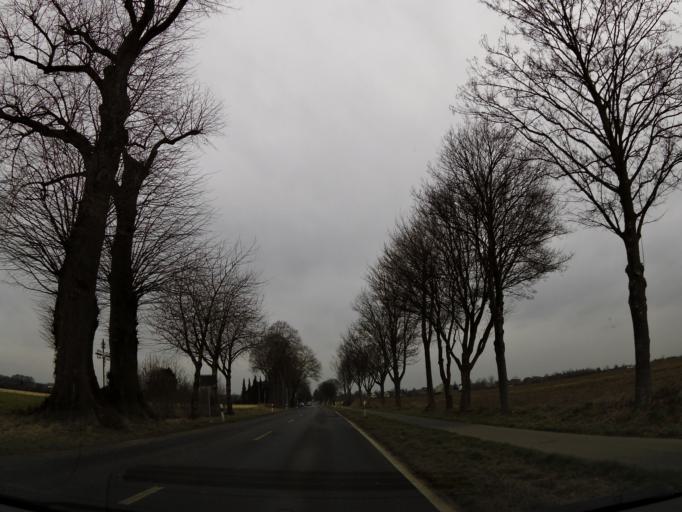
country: NL
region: Limburg
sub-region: Gemeente Schinnen
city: Doenrade
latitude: 50.9958
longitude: 5.9098
